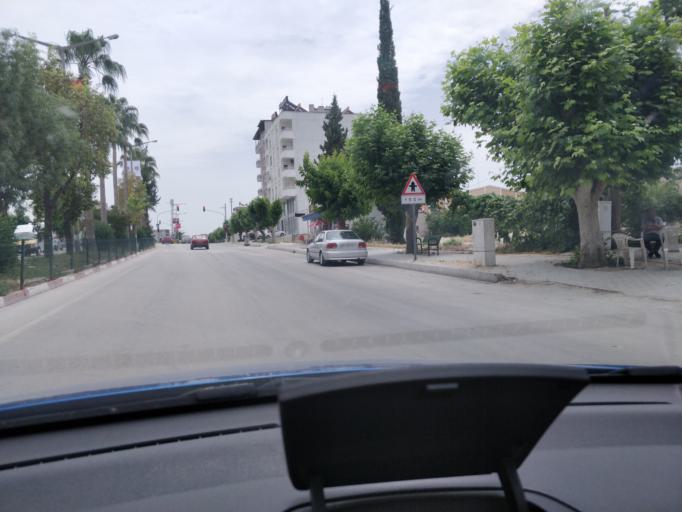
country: TR
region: Mersin
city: Mut
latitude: 36.6385
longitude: 33.4438
